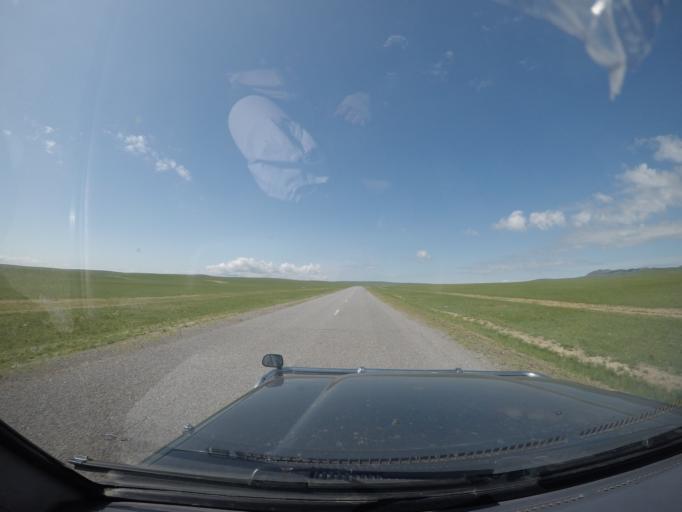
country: MN
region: Hentiy
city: Bayan
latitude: 47.3182
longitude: 111.3889
